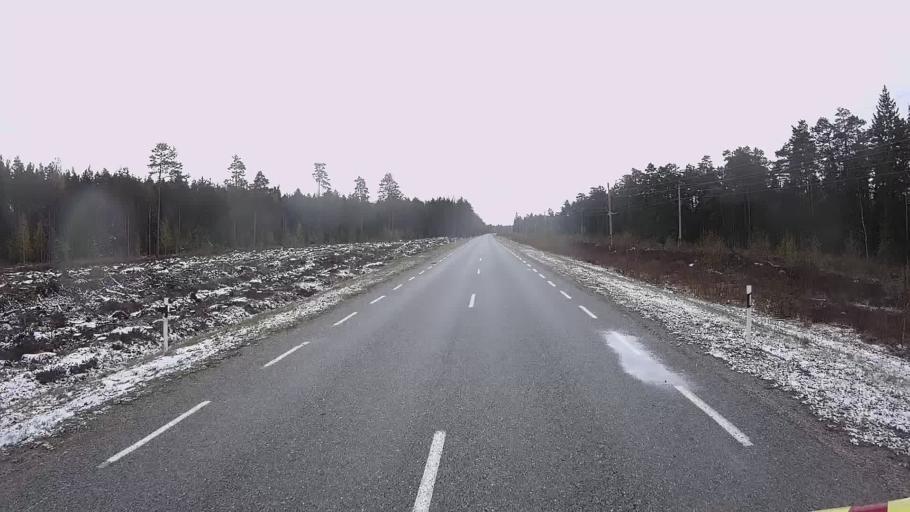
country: EE
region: Hiiumaa
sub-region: Kaerdla linn
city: Kardla
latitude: 59.0237
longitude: 22.6720
